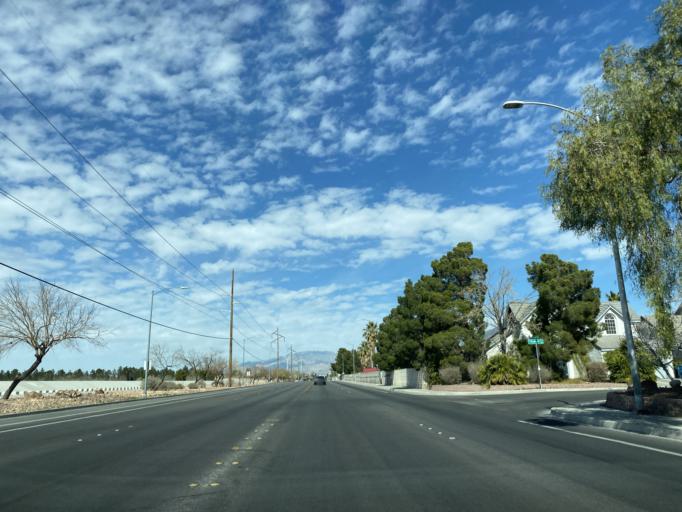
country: US
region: Nevada
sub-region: Clark County
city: Spring Valley
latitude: 36.2277
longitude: -115.2514
